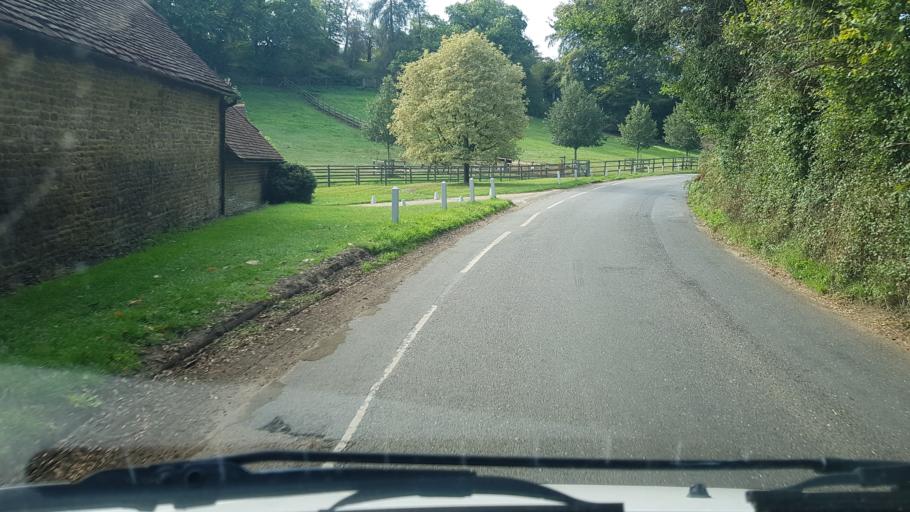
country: GB
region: England
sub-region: Surrey
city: Godalming
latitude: 51.2192
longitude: -0.6311
